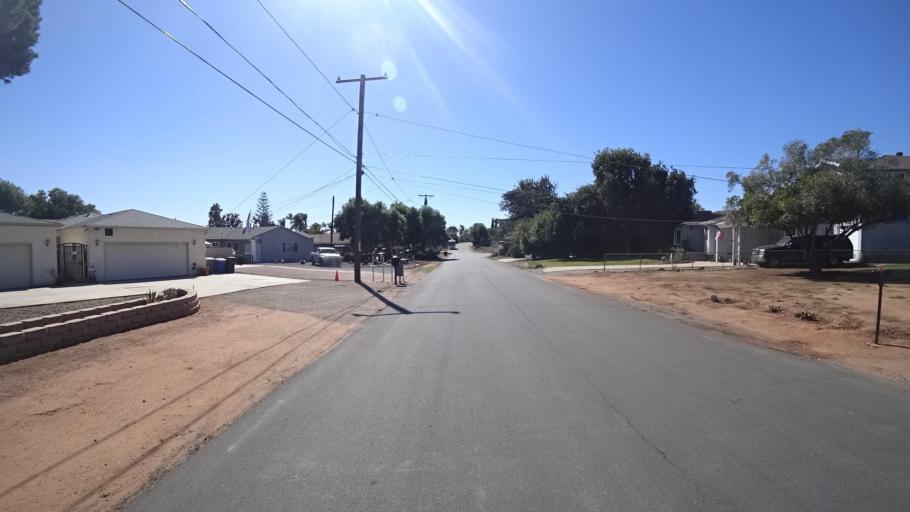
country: US
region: California
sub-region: San Diego County
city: Bonita
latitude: 32.6538
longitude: -117.0543
